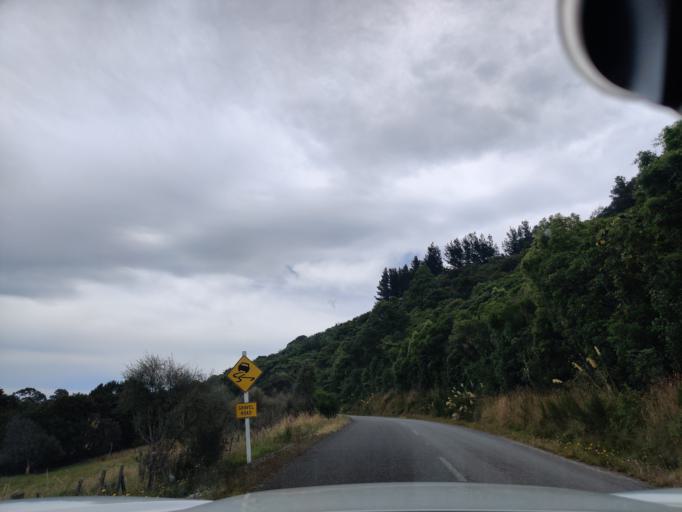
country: NZ
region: Wellington
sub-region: Masterton District
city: Masterton
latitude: -41.0376
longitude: 175.4169
